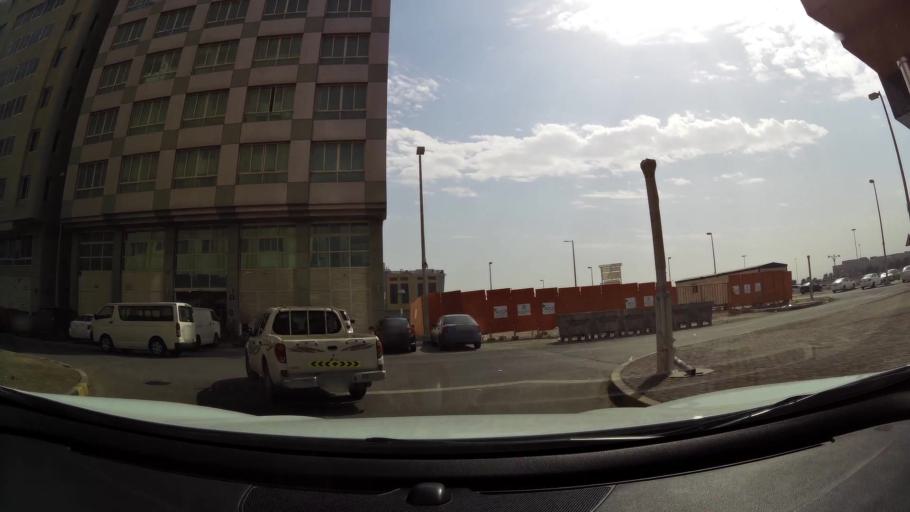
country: AE
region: Abu Dhabi
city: Abu Dhabi
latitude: 24.3340
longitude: 54.5308
